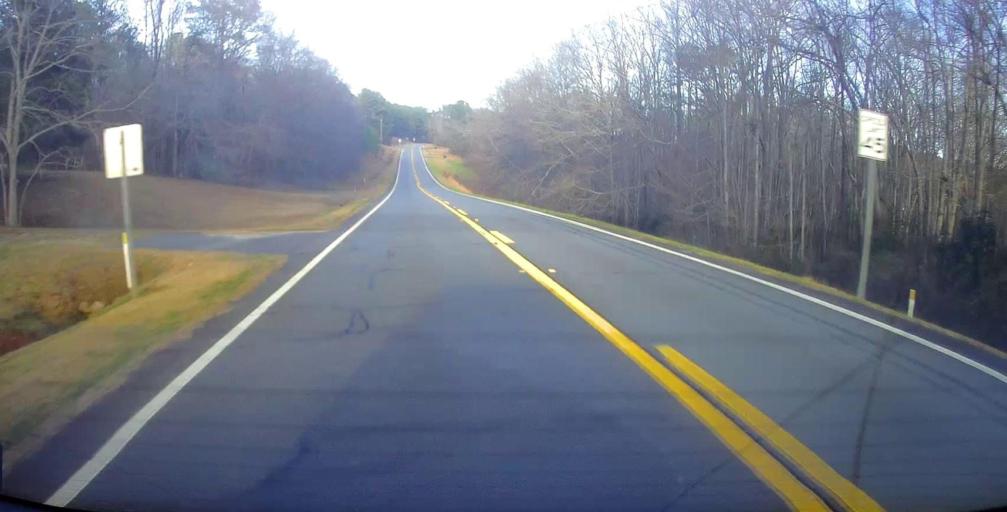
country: US
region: Georgia
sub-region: Talbot County
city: Sardis
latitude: 32.7891
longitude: -84.5565
